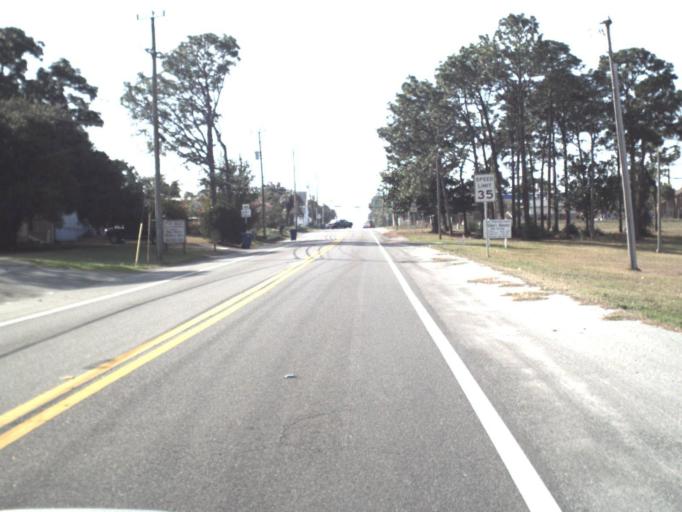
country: US
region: Florida
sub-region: Bay County
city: Pretty Bayou
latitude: 30.1920
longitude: -85.6835
